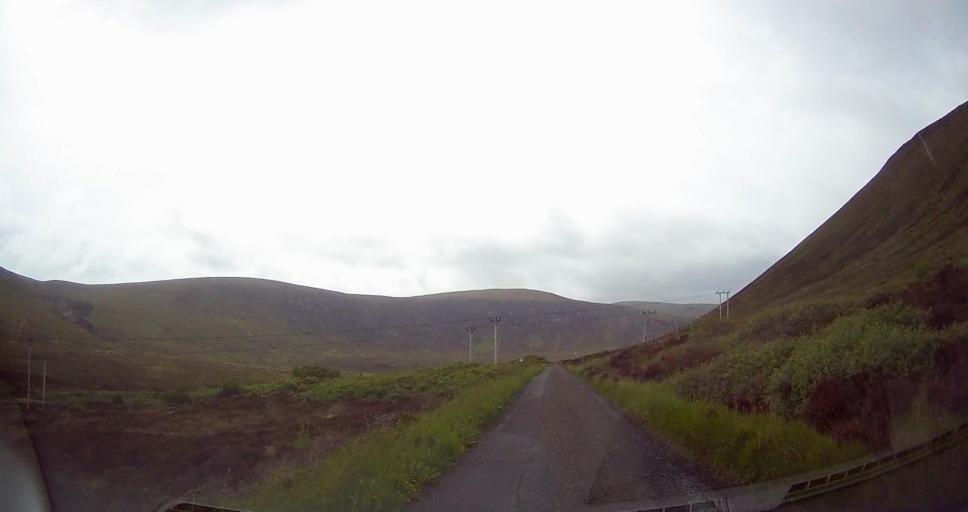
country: GB
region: Scotland
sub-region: Orkney Islands
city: Stromness
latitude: 58.8982
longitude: -3.3146
